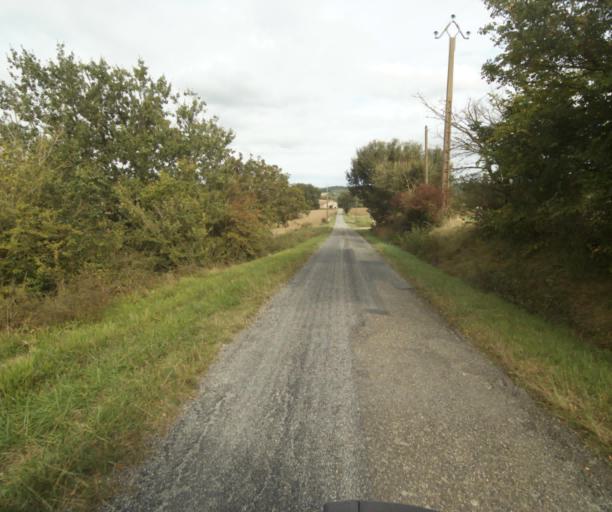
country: FR
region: Midi-Pyrenees
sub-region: Departement du Tarn-et-Garonne
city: Beaumont-de-Lomagne
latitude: 43.8241
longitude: 1.0771
